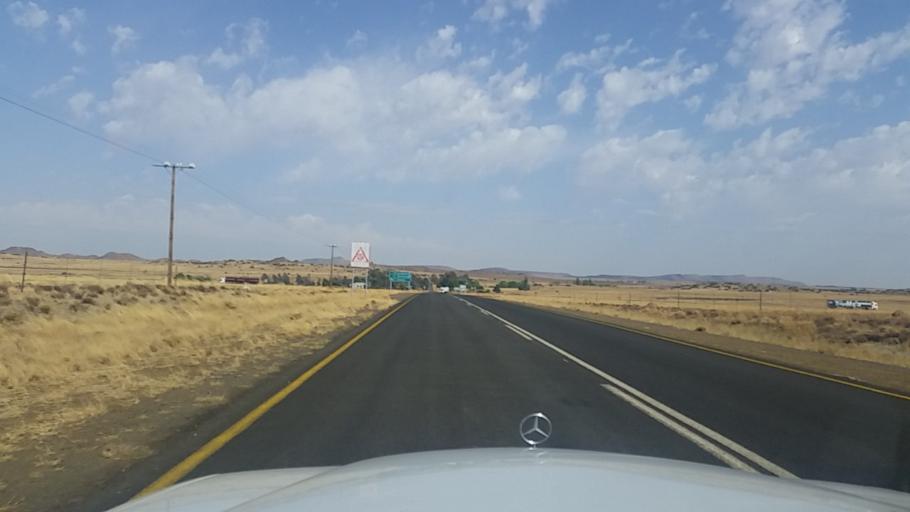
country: ZA
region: Orange Free State
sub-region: Xhariep District Municipality
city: Trompsburg
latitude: -30.2953
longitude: 25.7276
